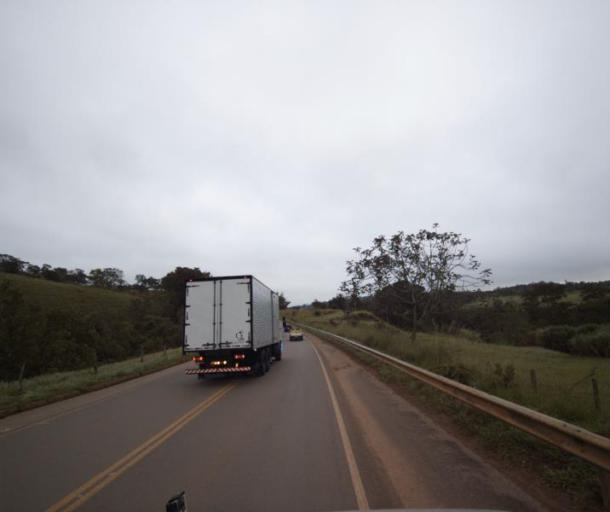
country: BR
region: Goias
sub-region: Pirenopolis
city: Pirenopolis
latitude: -15.9495
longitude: -48.8036
